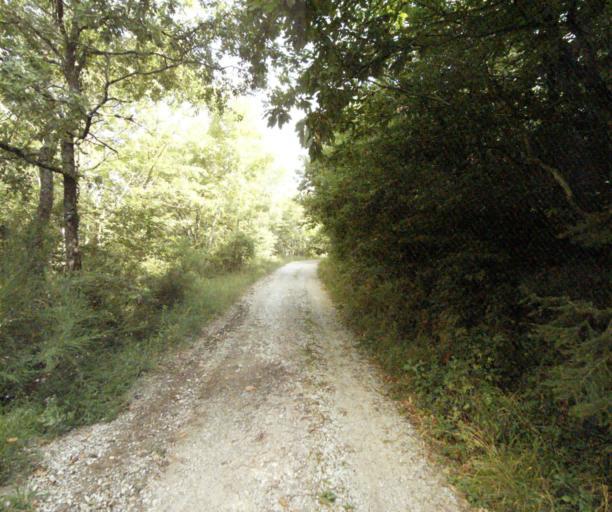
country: FR
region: Midi-Pyrenees
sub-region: Departement du Tarn
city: Dourgne
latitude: 43.4603
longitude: 2.1115
